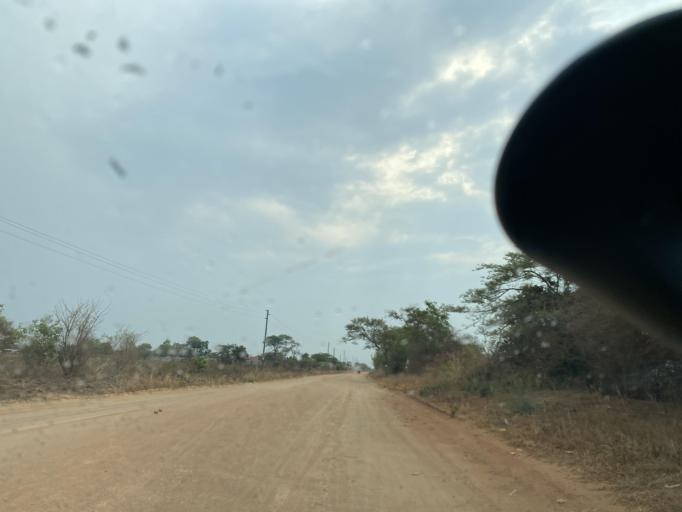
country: ZM
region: Lusaka
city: Lusaka
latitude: -15.2882
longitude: 28.2877
